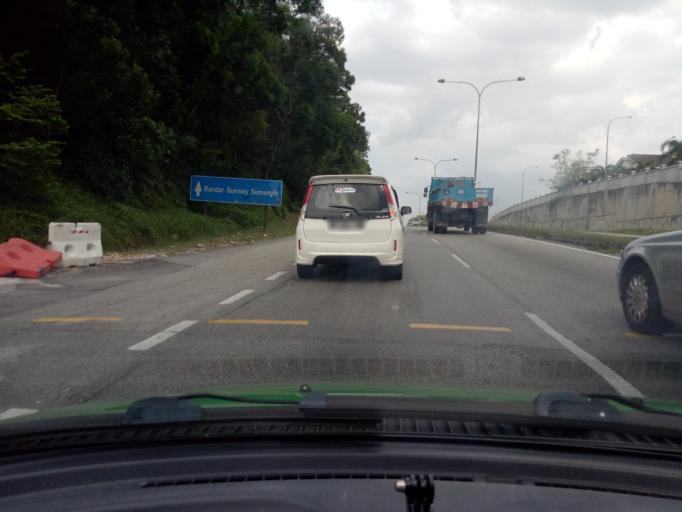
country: MY
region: Selangor
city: Kampong Baharu Balakong
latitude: 3.0044
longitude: 101.8066
